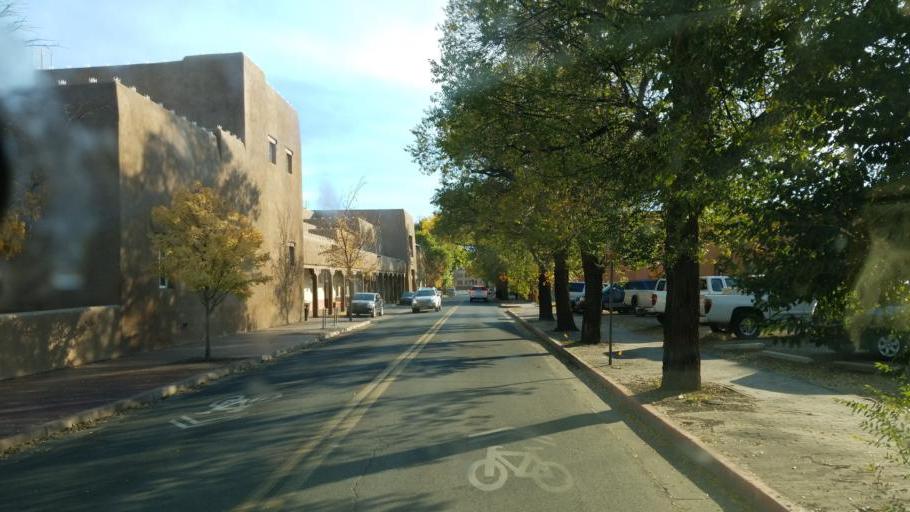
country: US
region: New Mexico
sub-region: Santa Fe County
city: Santa Fe
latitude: 35.6910
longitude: -105.9400
